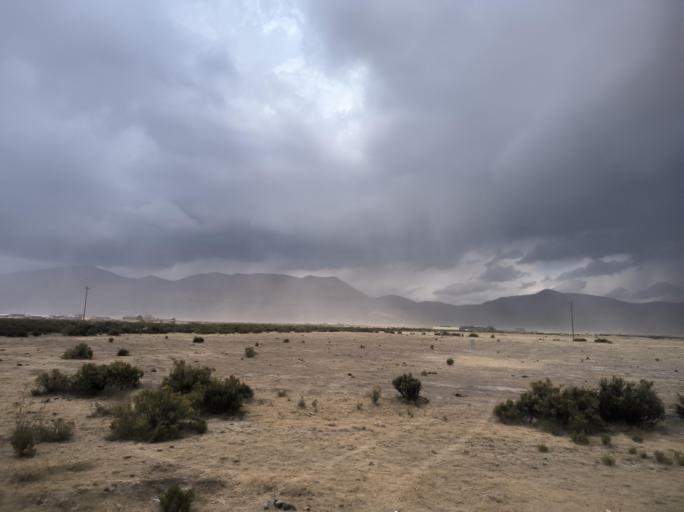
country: BO
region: Oruro
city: Challapata
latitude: -18.7748
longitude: -66.8540
